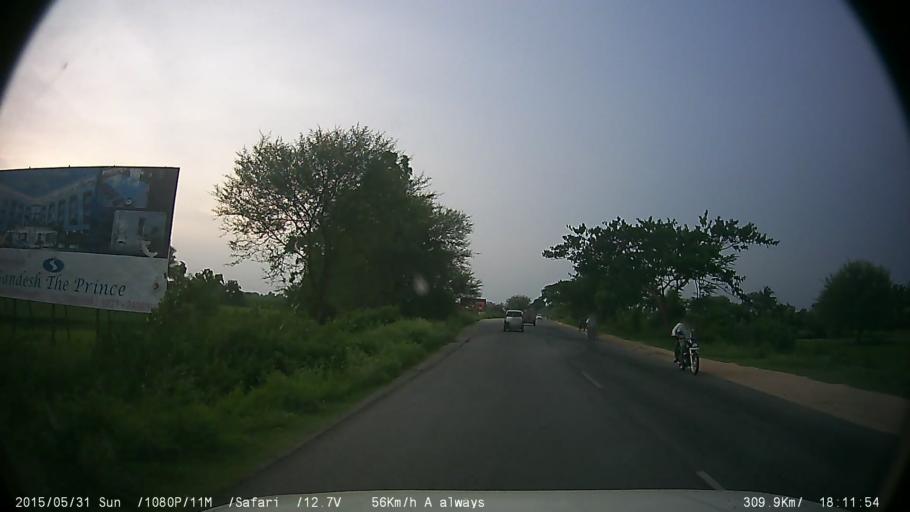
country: IN
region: Karnataka
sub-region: Mysore
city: Nanjangud
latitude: 12.0917
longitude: 76.6732
